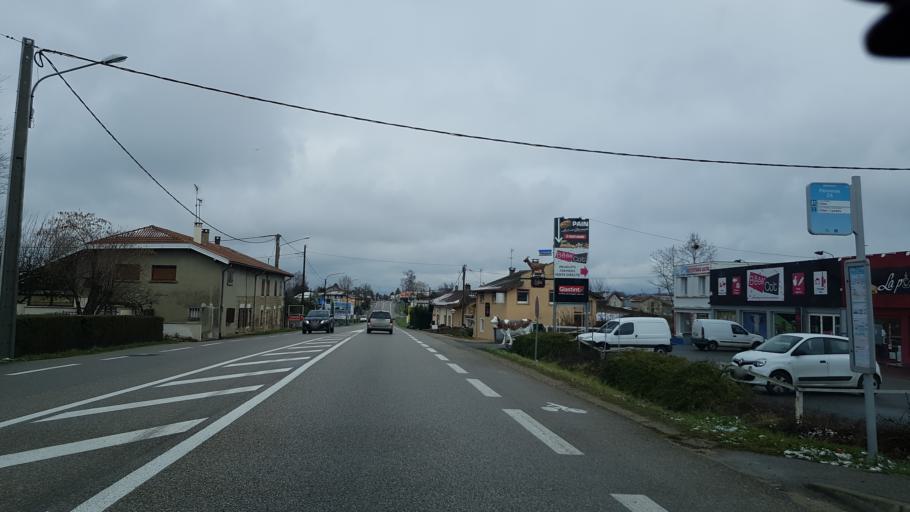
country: FR
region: Rhone-Alpes
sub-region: Departement de l'Ain
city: Peronnas
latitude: 46.1718
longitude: 5.1973
